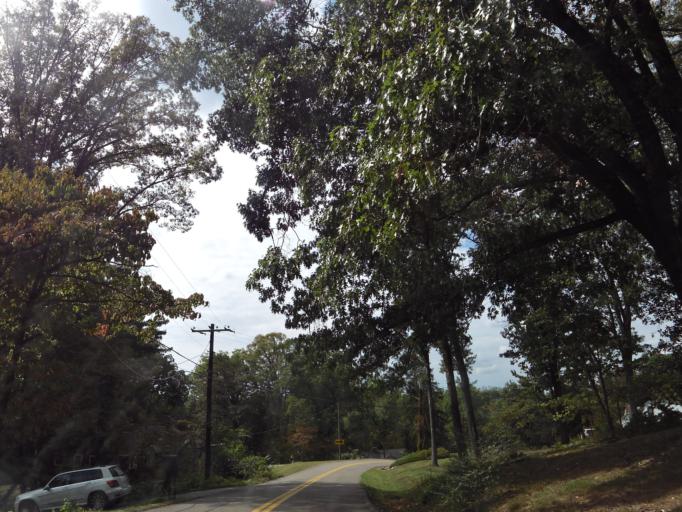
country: US
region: Tennessee
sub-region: Knox County
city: Knoxville
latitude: 35.9997
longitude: -83.8463
